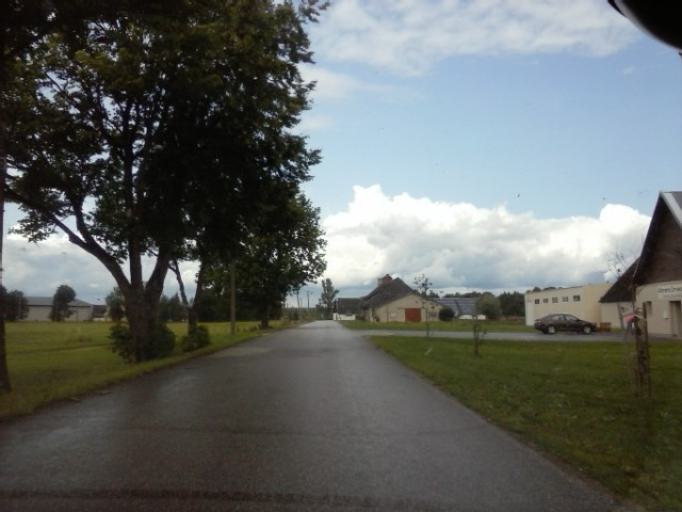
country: EE
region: Tartu
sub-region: Tartu linn
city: Tartu
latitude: 58.3574
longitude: 26.8792
